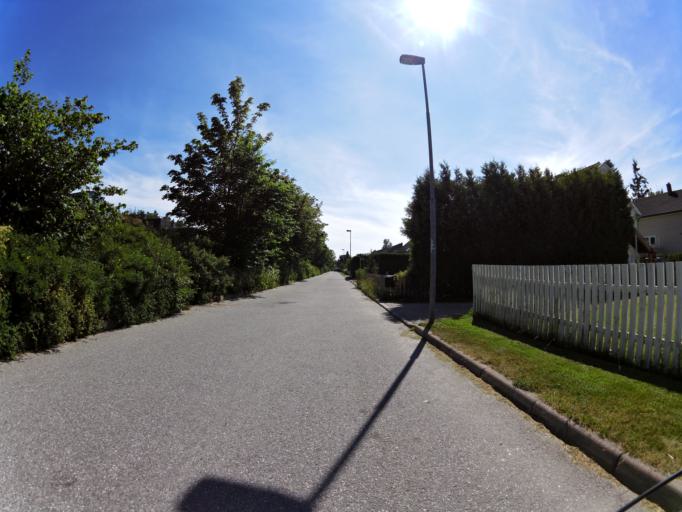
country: NO
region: Ostfold
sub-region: Fredrikstad
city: Fredrikstad
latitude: 59.2234
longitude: 10.9514
